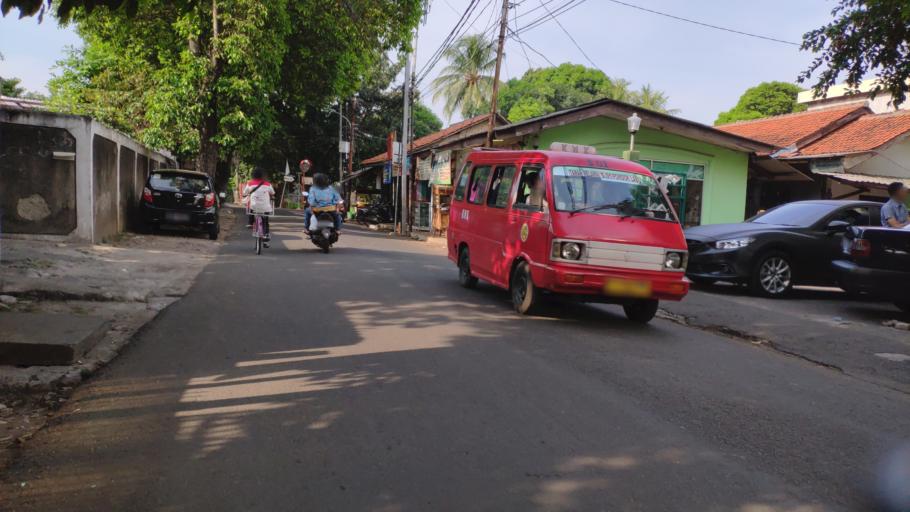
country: ID
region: West Java
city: Pamulang
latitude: -6.3080
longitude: 106.7988
